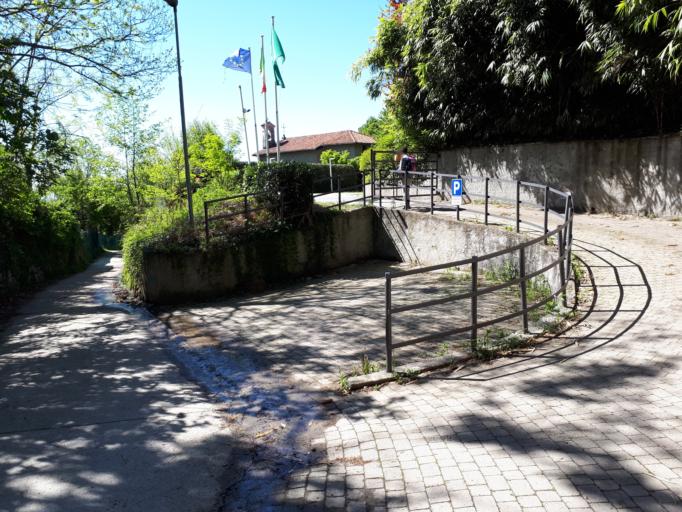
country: IT
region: Lombardy
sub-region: Provincia di Como
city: Cavallasca
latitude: 45.8168
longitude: 9.0239
